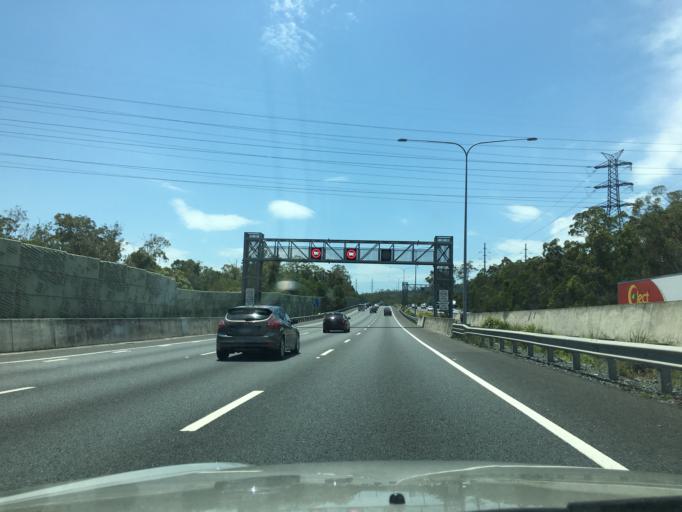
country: AU
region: Queensland
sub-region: Brisbane
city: Mackenzie
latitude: -27.5373
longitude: 153.1195
